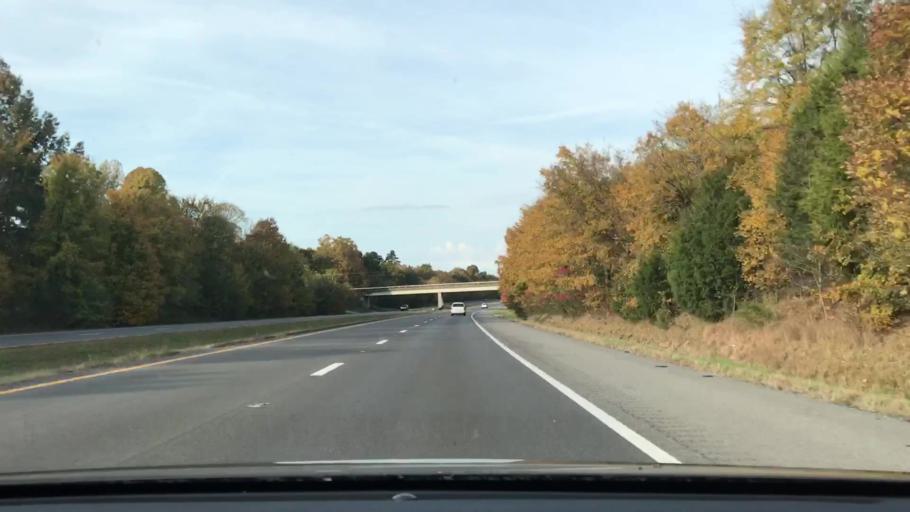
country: US
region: Kentucky
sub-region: Graves County
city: Mayfield
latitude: 36.7713
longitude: -88.6080
